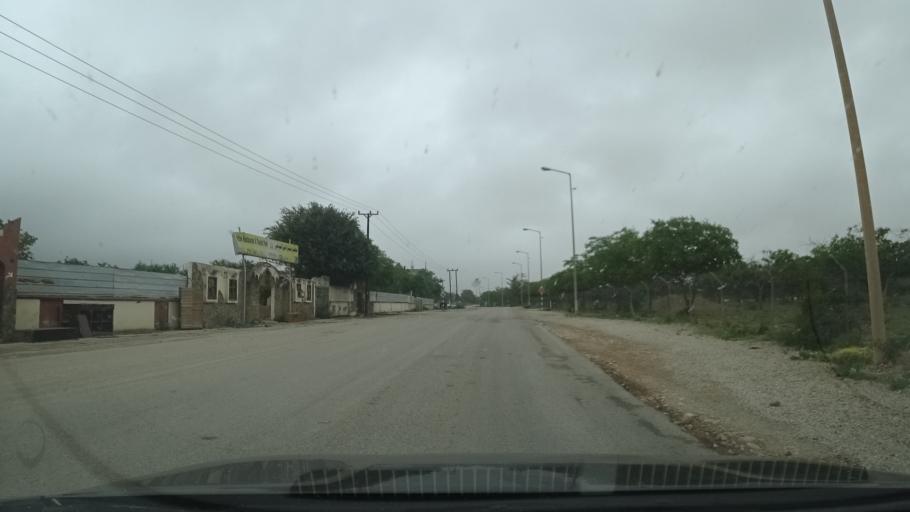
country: OM
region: Zufar
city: Salalah
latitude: 17.0856
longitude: 54.0712
